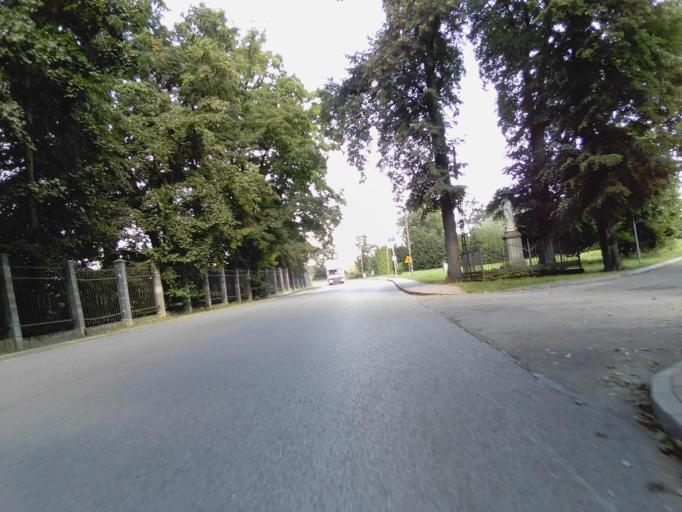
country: PL
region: Subcarpathian Voivodeship
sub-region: Powiat krosnienski
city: Jedlicze
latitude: 49.7135
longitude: 21.6381
